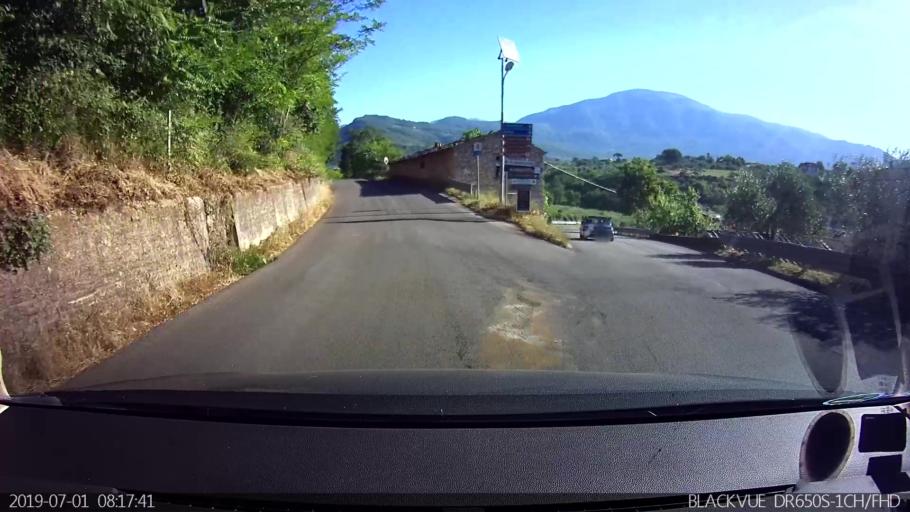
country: IT
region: Latium
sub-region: Provincia di Frosinone
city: Veroli
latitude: 41.7081
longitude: 13.4401
